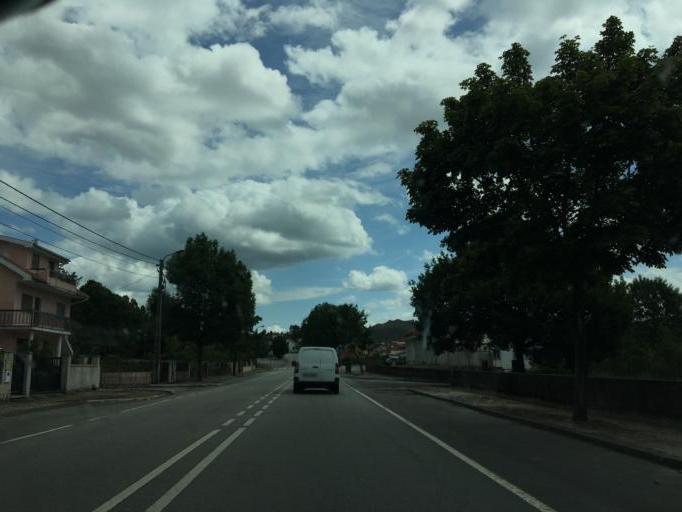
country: PT
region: Vila Real
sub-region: Boticas
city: Boticas
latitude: 41.6925
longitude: -7.6554
